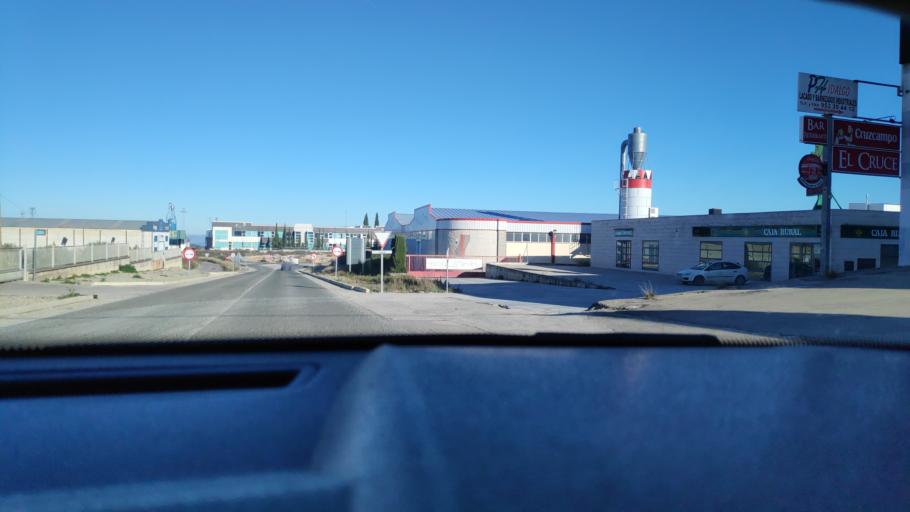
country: ES
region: Andalusia
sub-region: Provincia de Jaen
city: Mancha Real
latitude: 37.8055
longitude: -3.6116
